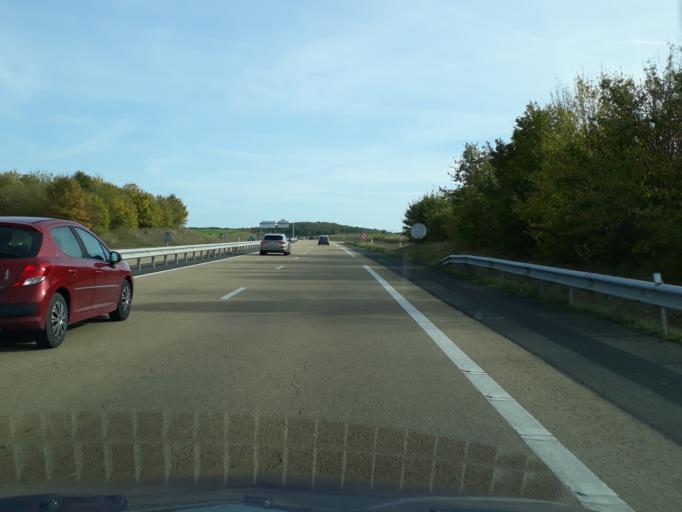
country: FR
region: Champagne-Ardenne
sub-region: Departement de l'Aube
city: Aix-en-Othe
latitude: 48.2407
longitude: 3.5990
